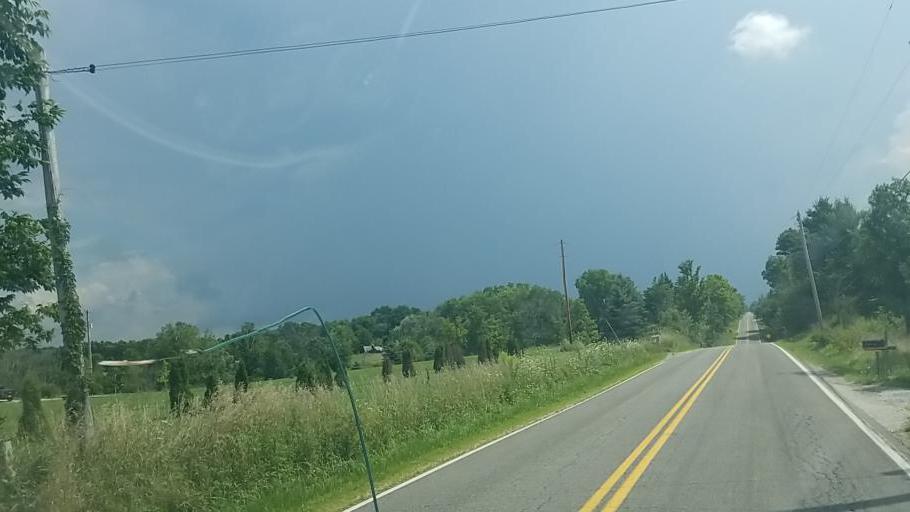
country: US
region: Ohio
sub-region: Medina County
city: Lodi
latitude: 41.0872
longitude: -82.0043
